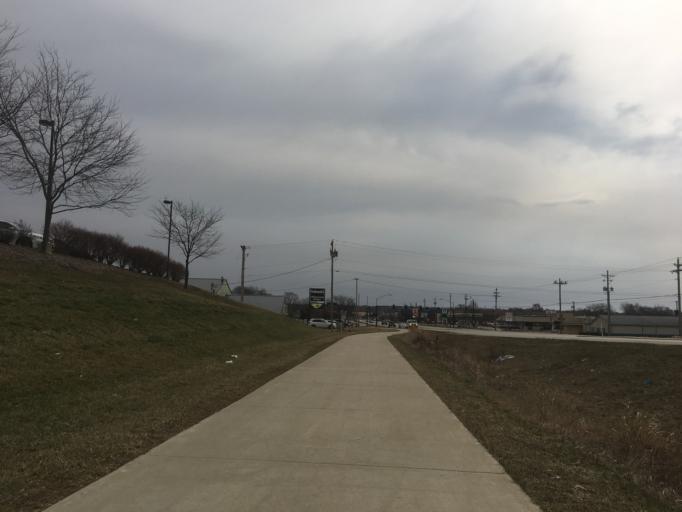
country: US
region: Iowa
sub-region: Johnson County
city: University Heights
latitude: 41.6476
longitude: -91.5487
